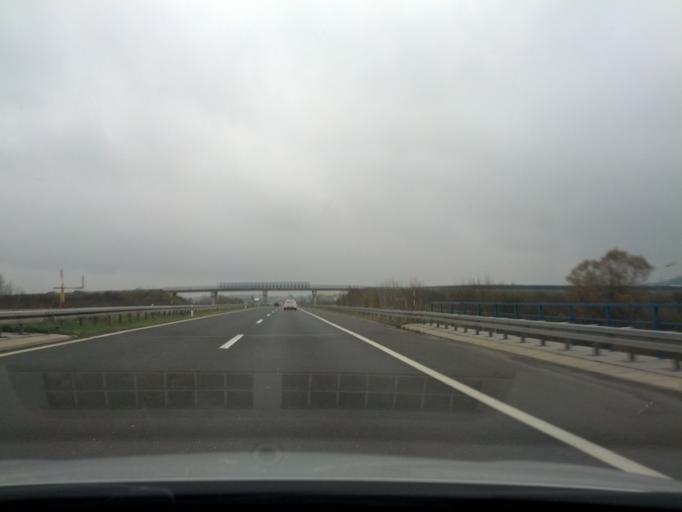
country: HR
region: Zagrebacka
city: Bestovje
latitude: 45.8090
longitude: 15.7692
